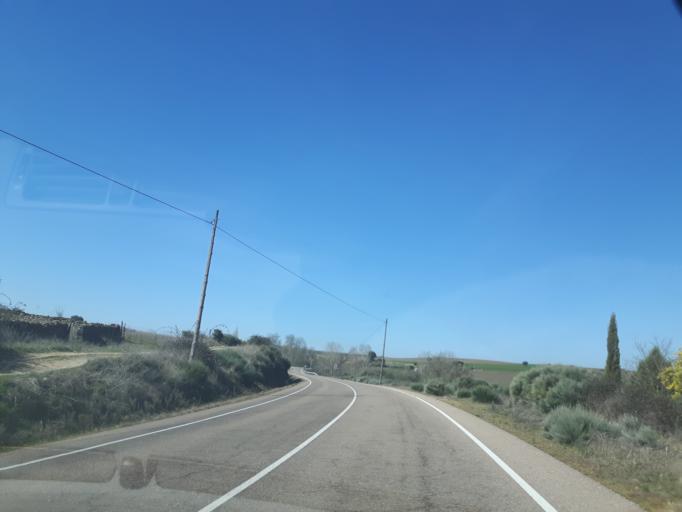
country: ES
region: Castille and Leon
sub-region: Provincia de Salamanca
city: Cerralbo
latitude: 40.9728
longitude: -6.5938
